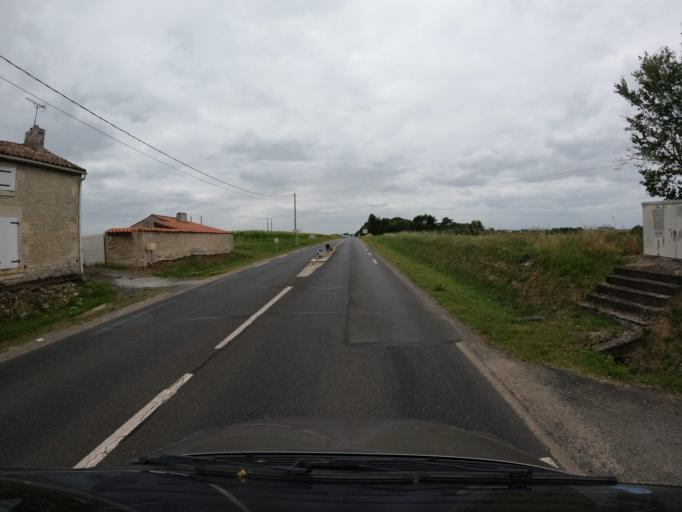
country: FR
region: Pays de la Loire
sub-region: Departement de la Vendee
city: Saint-Hilaire-des-Loges
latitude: 46.4041
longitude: -0.6740
